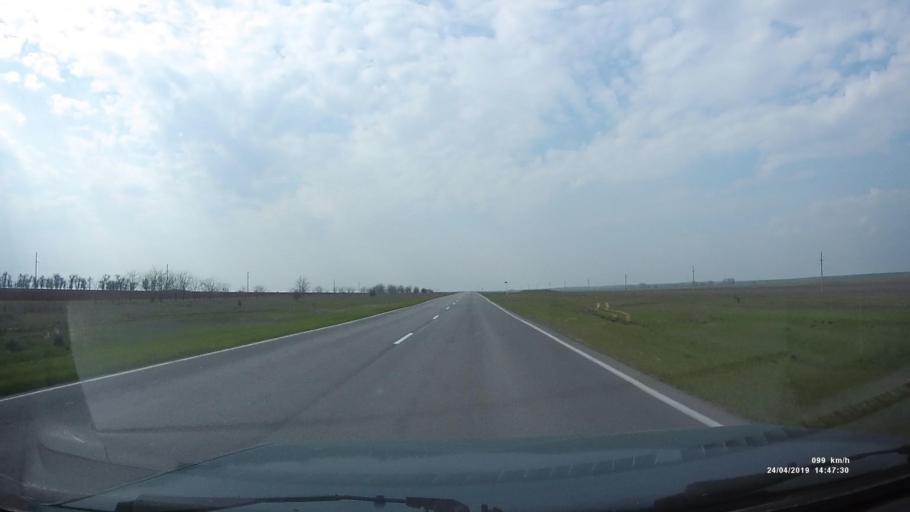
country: RU
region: Rostov
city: Remontnoye
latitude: 46.4929
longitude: 43.7710
